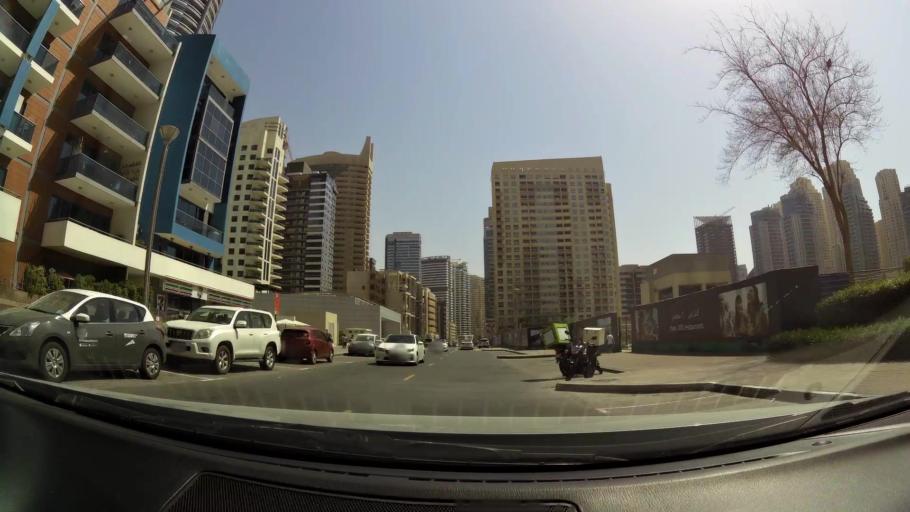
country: AE
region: Dubai
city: Dubai
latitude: 25.0729
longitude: 55.1370
